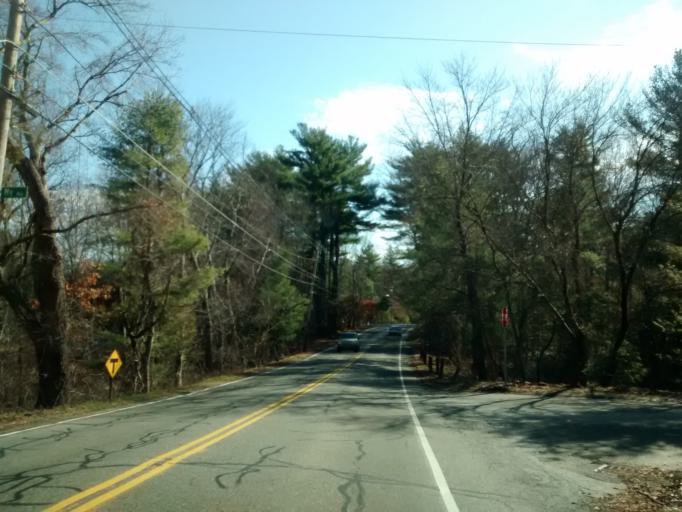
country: US
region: Massachusetts
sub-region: Worcester County
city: Uxbridge
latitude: 42.1019
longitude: -71.6109
